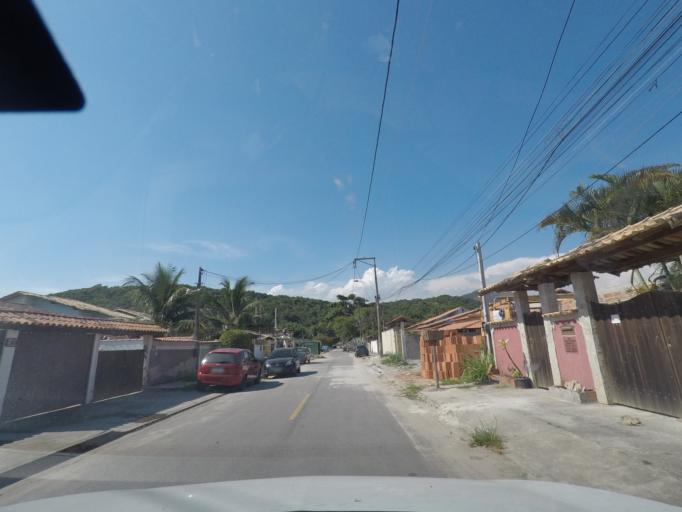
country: BR
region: Rio de Janeiro
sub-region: Niteroi
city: Niteroi
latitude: -22.9610
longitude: -42.9729
